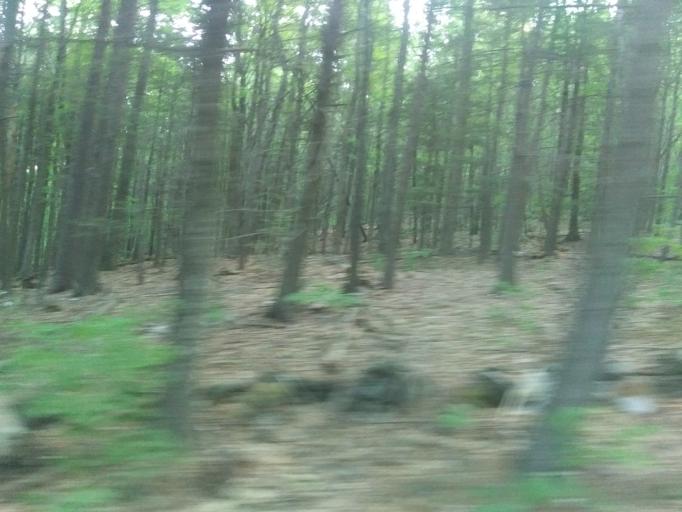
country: US
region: Massachusetts
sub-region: Franklin County
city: Buckland
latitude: 42.5709
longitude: -72.7695
